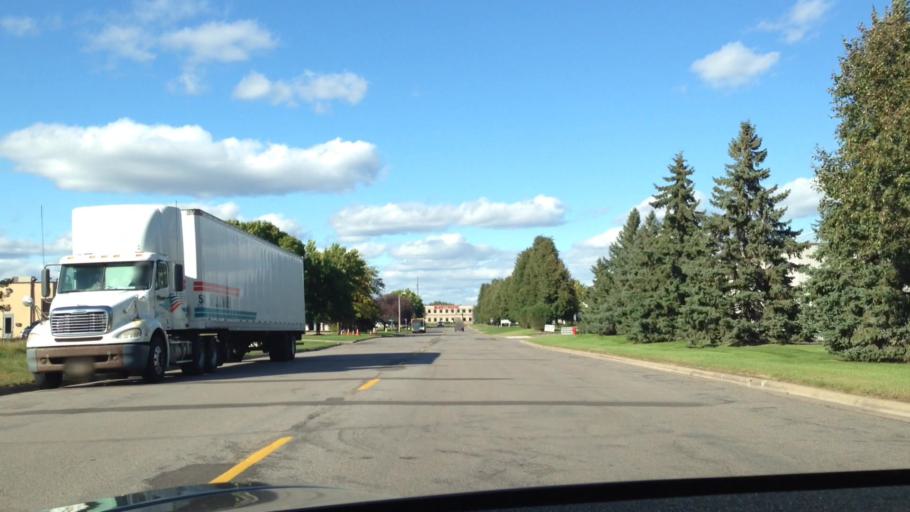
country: US
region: Minnesota
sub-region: Hennepin County
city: Osseo
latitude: 45.1126
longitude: -93.3869
